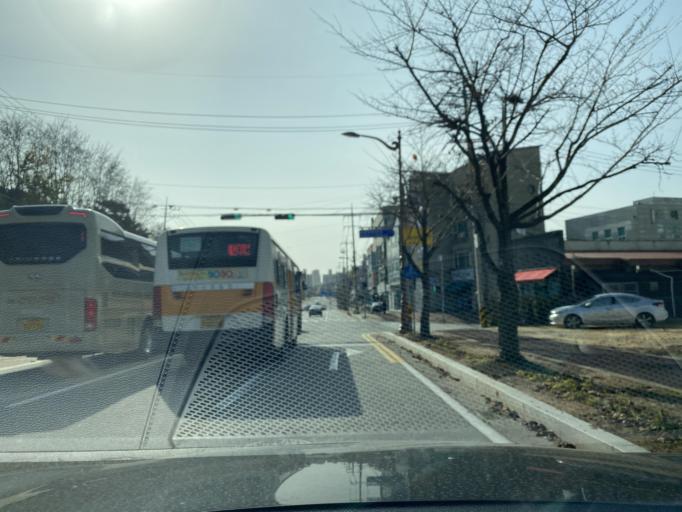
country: KR
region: Chungcheongnam-do
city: Yesan
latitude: 36.6949
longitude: 126.8366
